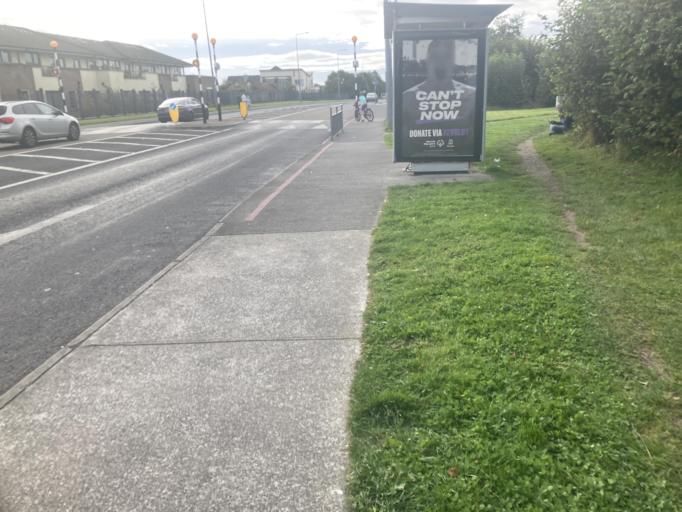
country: IE
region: Connaught
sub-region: County Galway
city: Bearna
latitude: 53.2674
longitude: -9.1208
